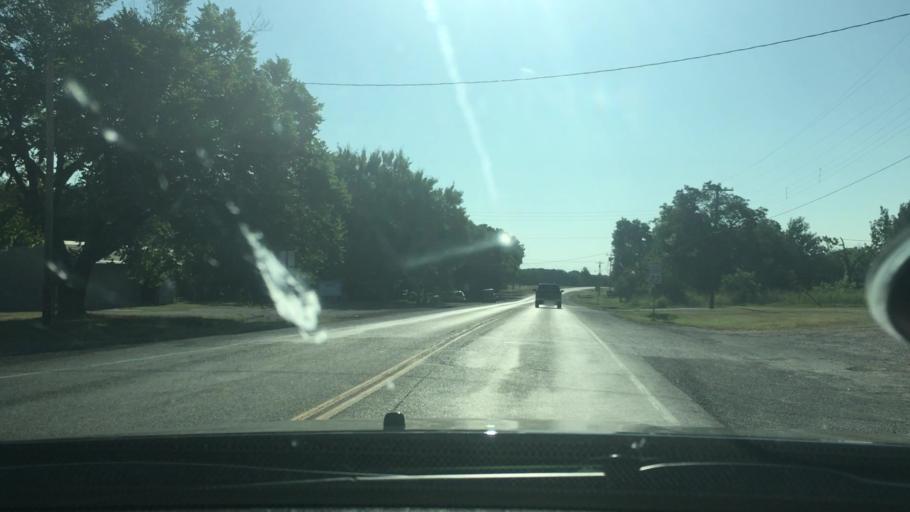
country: US
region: Oklahoma
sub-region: Johnston County
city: Tishomingo
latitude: 34.2414
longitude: -96.7514
